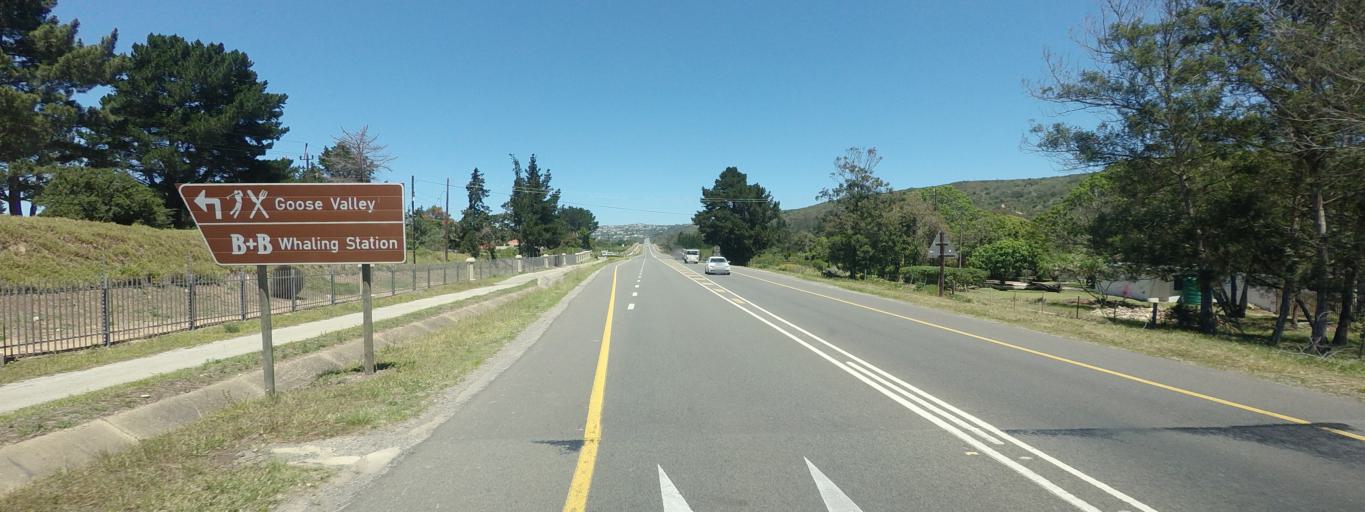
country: ZA
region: Western Cape
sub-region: Eden District Municipality
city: Plettenberg Bay
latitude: -34.0248
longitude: 23.3801
